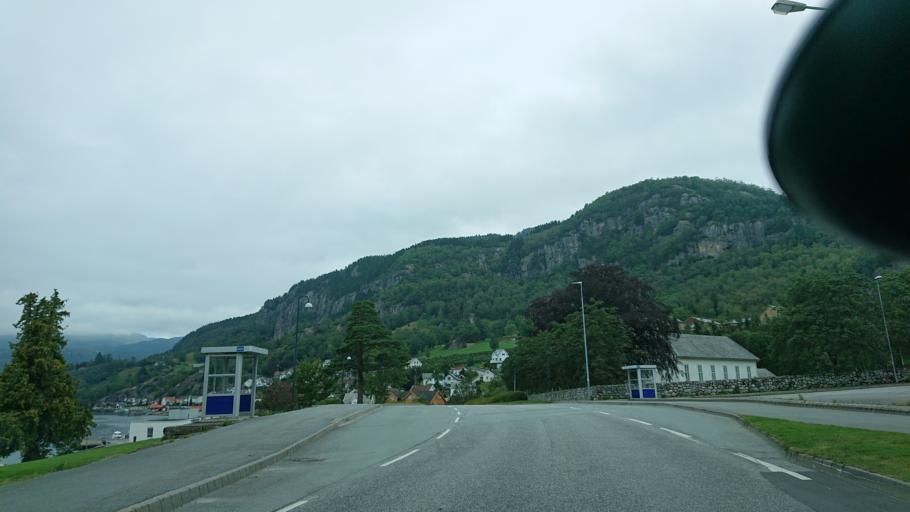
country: NO
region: Rogaland
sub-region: Hjelmeland
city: Hjelmelandsvagen
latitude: 59.2350
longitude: 6.1789
